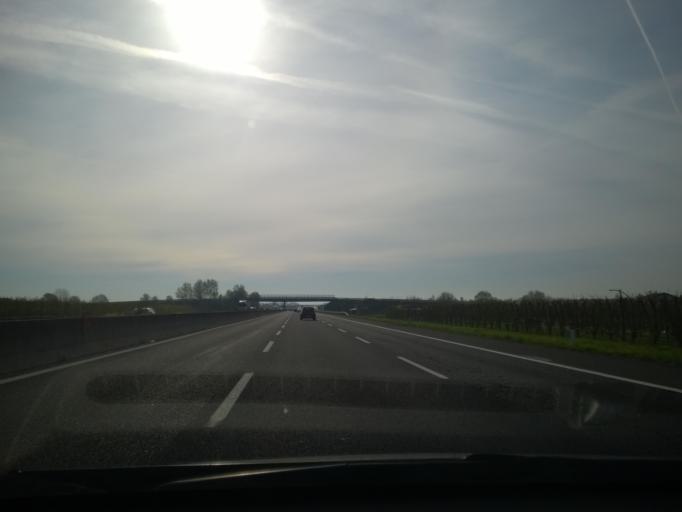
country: IT
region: Emilia-Romagna
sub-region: Provincia di Bologna
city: Bubano
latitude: 44.3713
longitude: 11.7681
